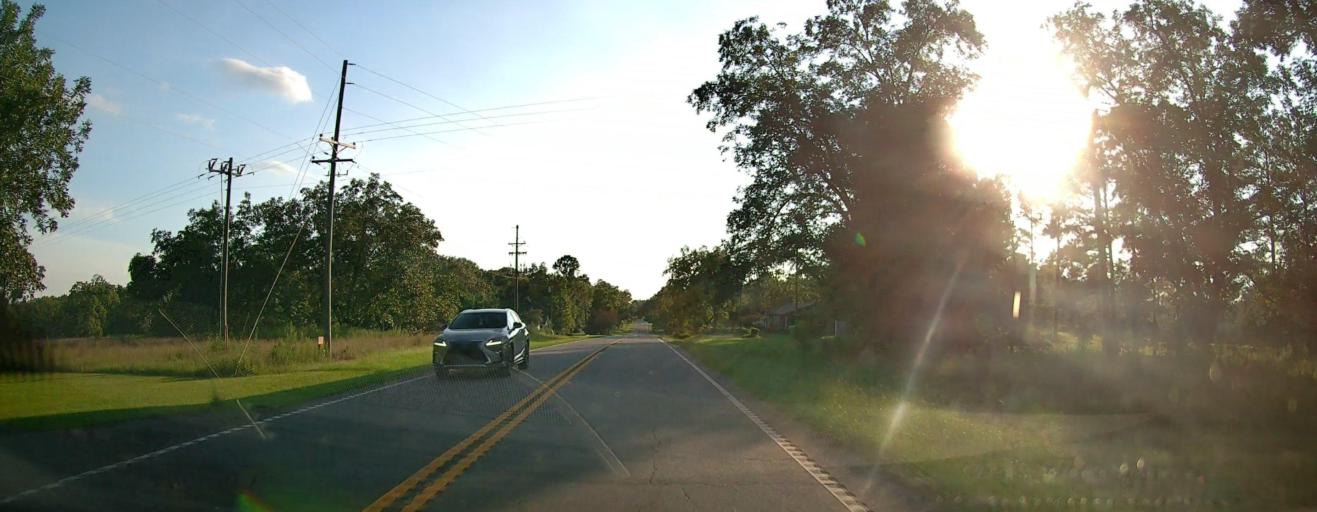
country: US
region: Georgia
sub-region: Crawford County
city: Roberta
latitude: 32.7110
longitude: -84.0247
